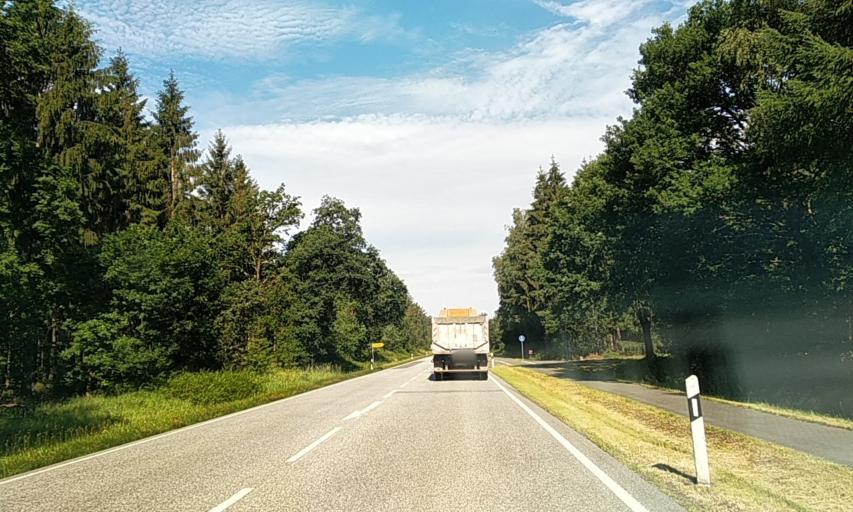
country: DE
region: Schleswig-Holstein
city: Owschlag
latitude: 54.3494
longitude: 9.5742
